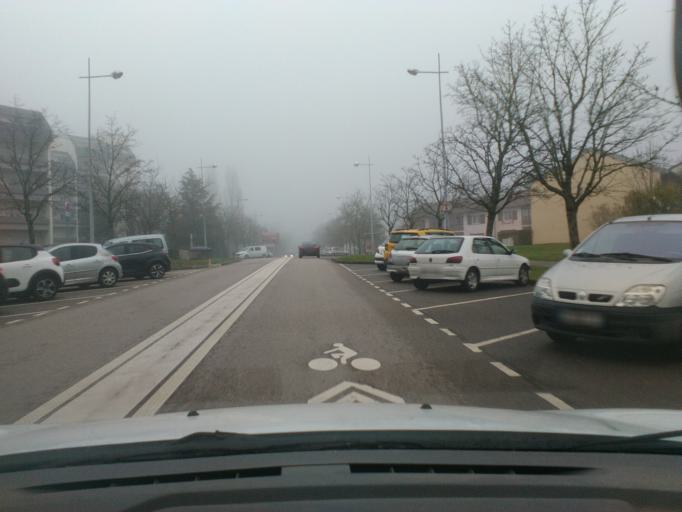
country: FR
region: Lorraine
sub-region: Departement des Vosges
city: Epinal
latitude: 48.1914
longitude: 6.4582
